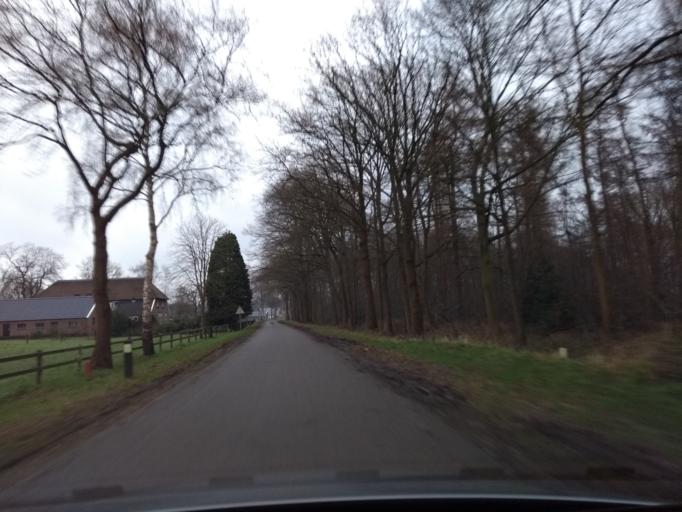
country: NL
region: Gelderland
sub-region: Gemeente Lochem
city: Harfsen
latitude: 52.2408
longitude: 6.3332
